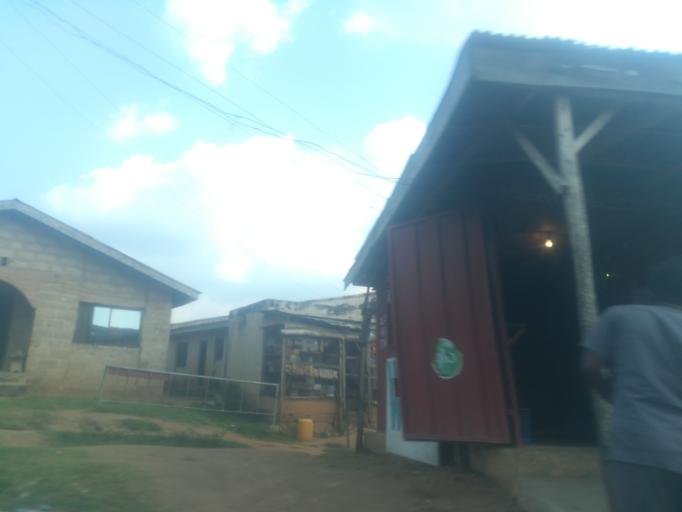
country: NG
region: Oyo
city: Moniya
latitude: 7.5114
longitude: 3.9057
